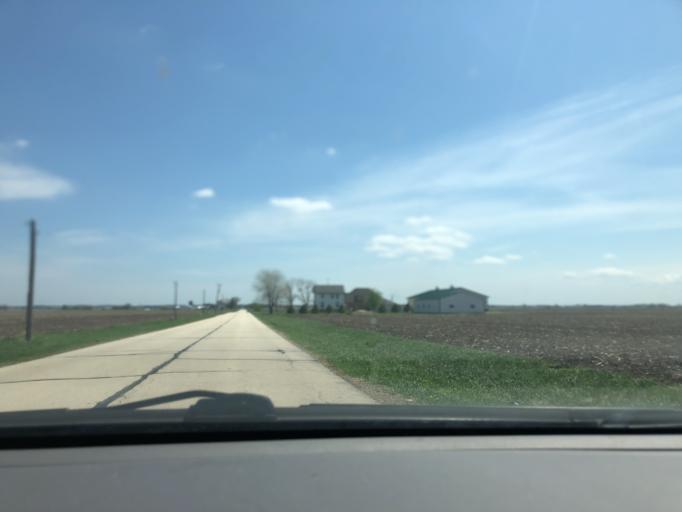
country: US
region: Illinois
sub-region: Kane County
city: Hampshire
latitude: 42.1099
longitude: -88.5957
